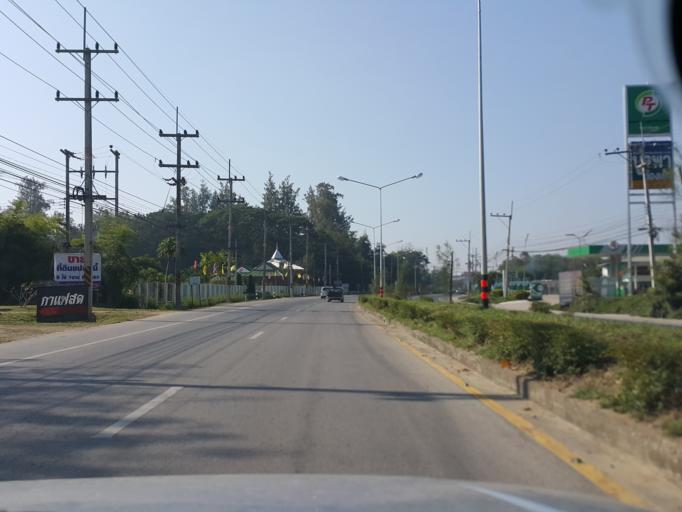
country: TH
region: Chiang Mai
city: San Pa Tong
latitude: 18.5726
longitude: 98.8791
